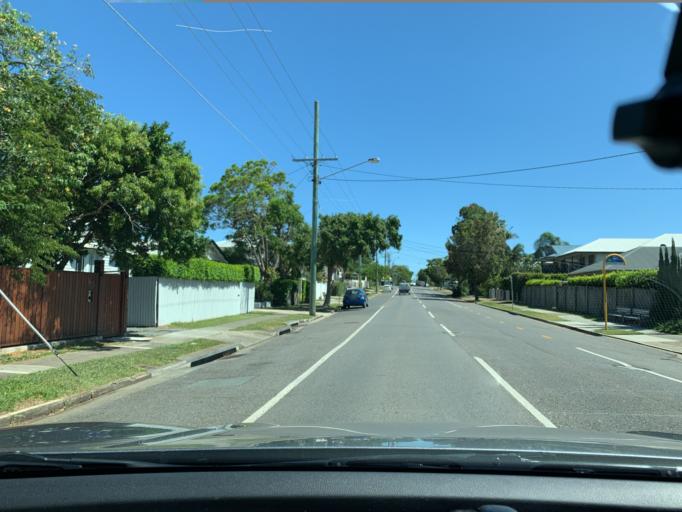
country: AU
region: Queensland
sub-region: Brisbane
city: Ascot
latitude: -27.4202
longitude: 153.0639
